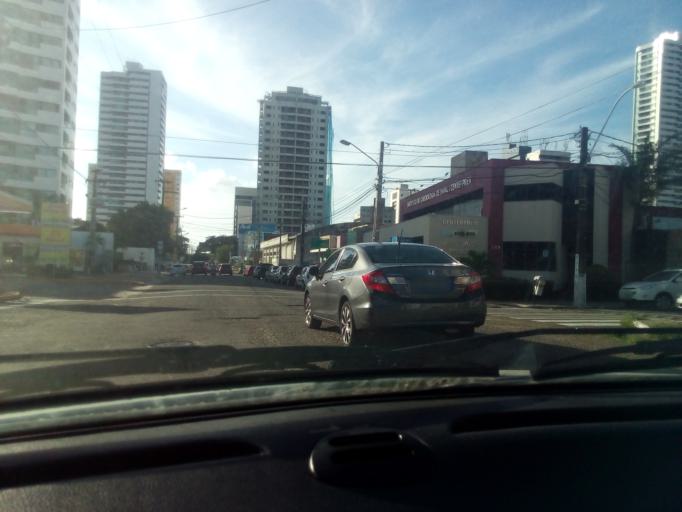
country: BR
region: Rio Grande do Norte
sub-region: Natal
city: Natal
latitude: -5.7914
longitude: -35.2010
